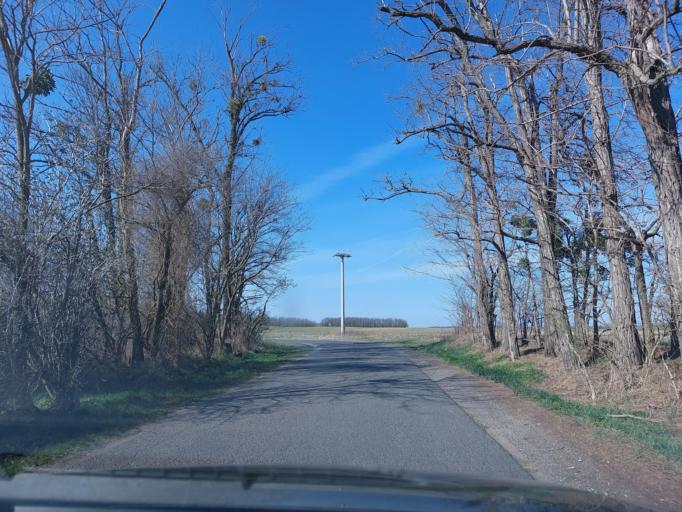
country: HU
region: Veszprem
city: Devecser
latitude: 47.1361
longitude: 17.3990
